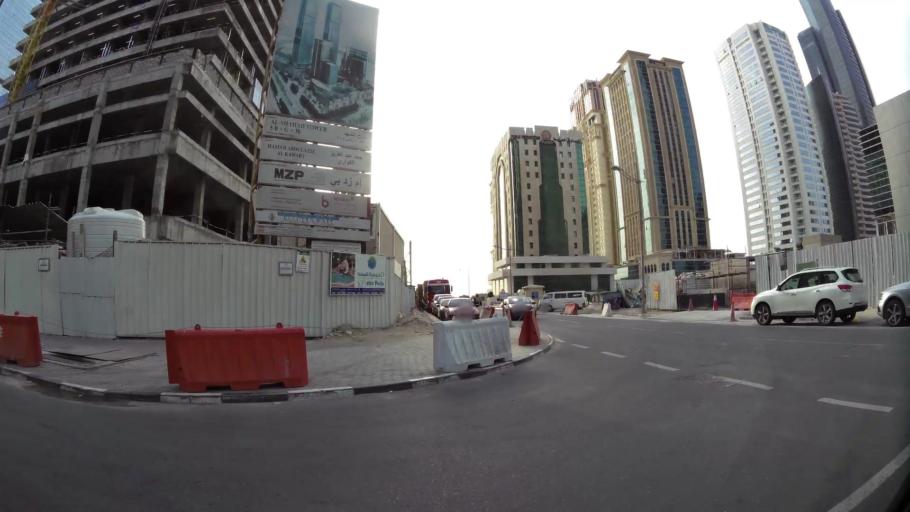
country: QA
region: Baladiyat ad Dawhah
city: Doha
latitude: 25.3238
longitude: 51.5259
